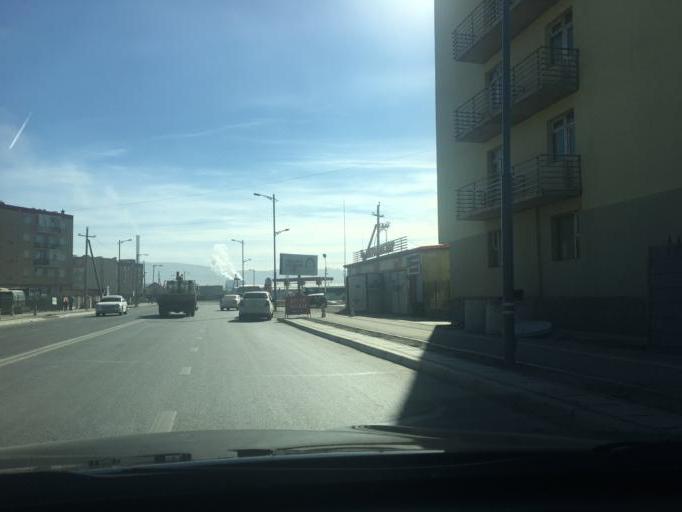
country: MN
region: Ulaanbaatar
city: Ulaanbaatar
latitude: 47.9120
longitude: 106.7833
